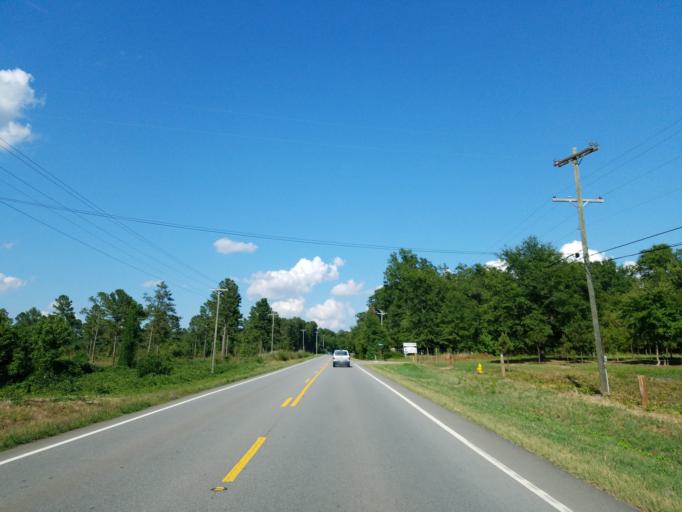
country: US
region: Georgia
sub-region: Peach County
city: Fort Valley
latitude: 32.5557
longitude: -83.8559
